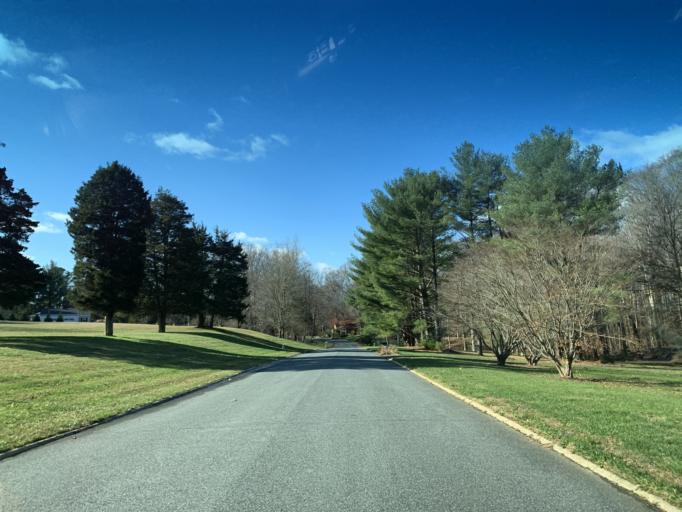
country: US
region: Maryland
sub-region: Harford County
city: South Bel Air
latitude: 39.5720
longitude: -76.2564
